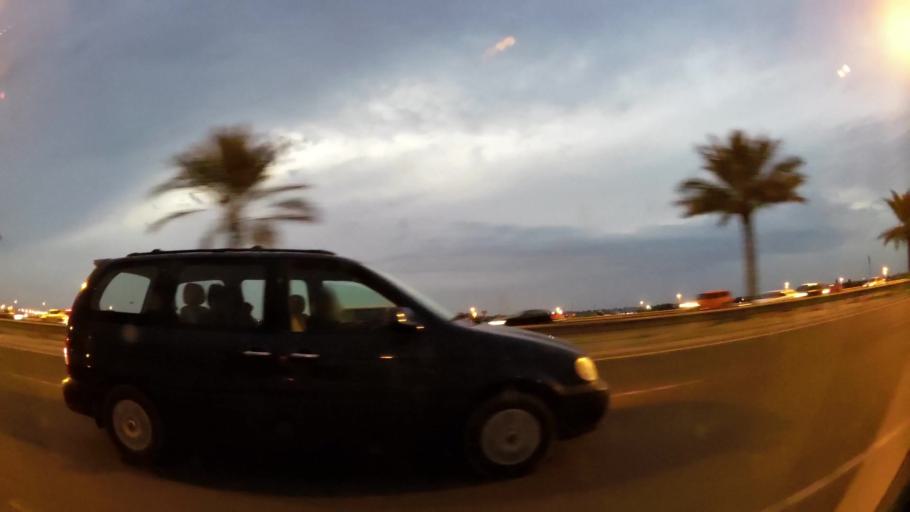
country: BH
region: Northern
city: Madinat `Isa
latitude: 26.1868
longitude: 50.5037
